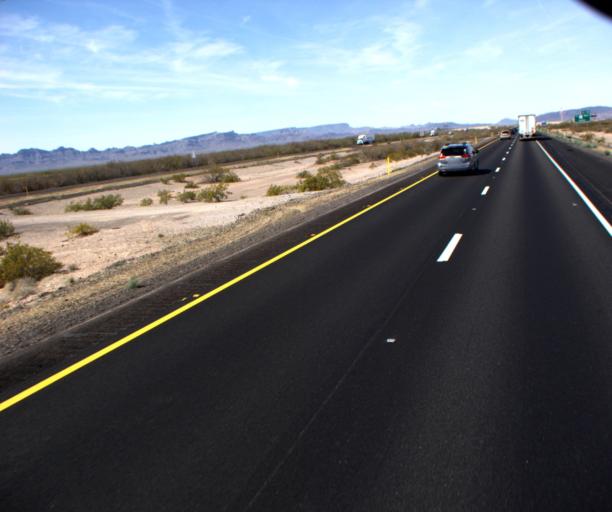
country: US
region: Arizona
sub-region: La Paz County
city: Salome
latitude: 33.6288
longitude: -113.7509
